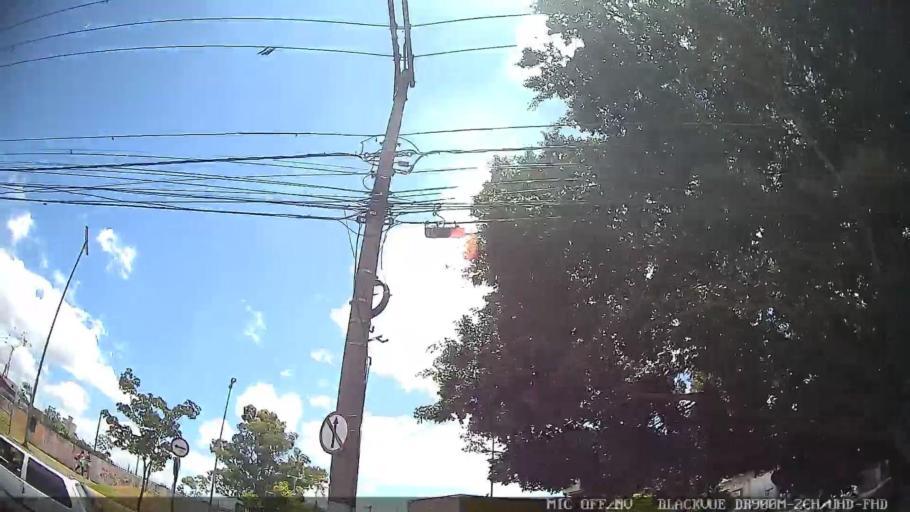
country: BR
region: Sao Paulo
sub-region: Diadema
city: Diadema
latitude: -23.6667
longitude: -46.6526
